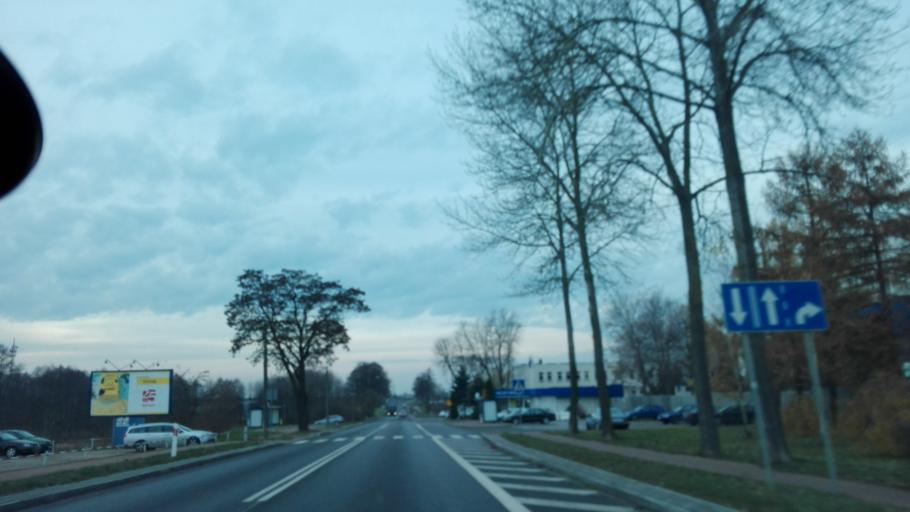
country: PL
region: Lublin Voivodeship
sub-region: Powiat radzynski
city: Radzyn Podlaski
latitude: 51.7739
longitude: 22.5986
